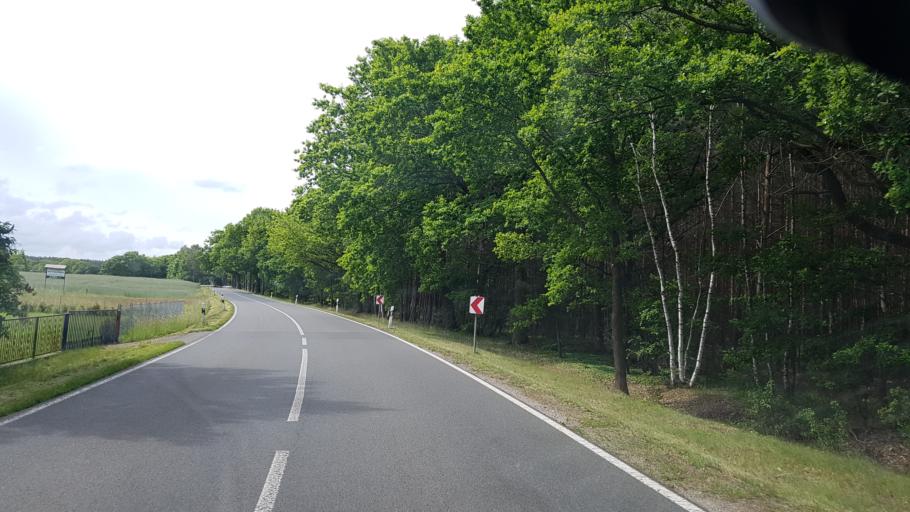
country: DE
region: Brandenburg
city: Sonnewalde
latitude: 51.7536
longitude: 13.6782
